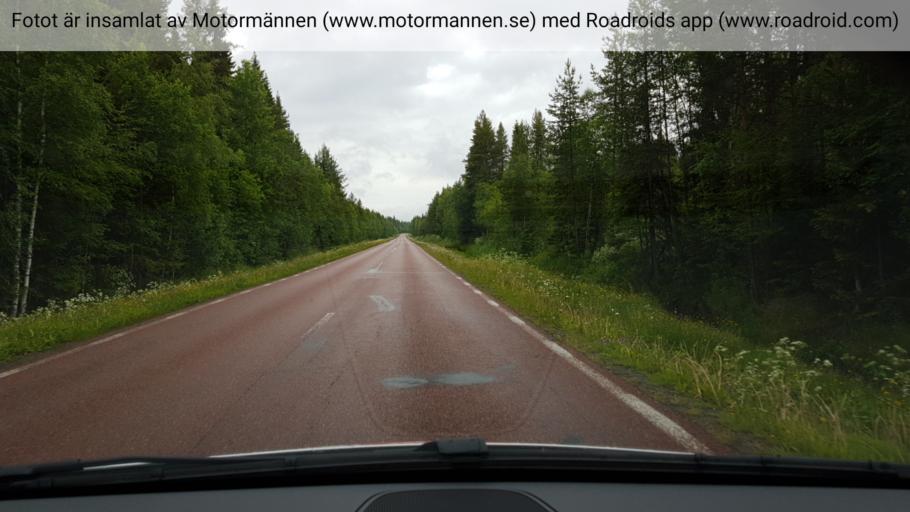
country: SE
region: Vaesterbotten
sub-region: Dorotea Kommun
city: Dorotea
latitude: 64.0837
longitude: 16.0865
